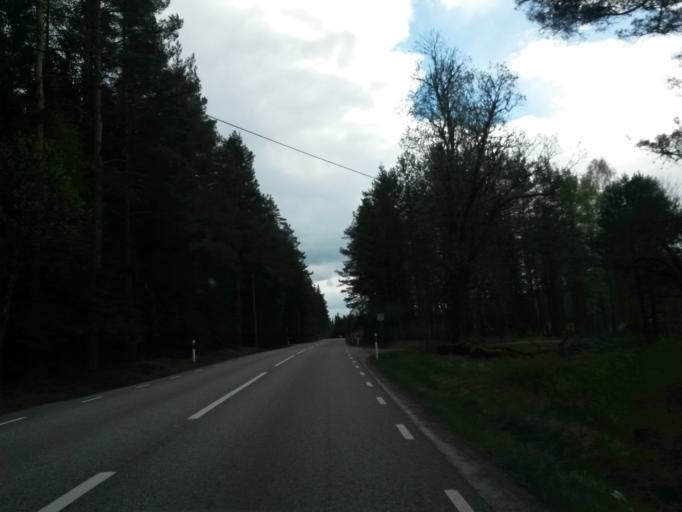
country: SE
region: Vaestra Goetaland
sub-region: Boras Kommun
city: Boras
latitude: 57.8860
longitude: 12.9293
